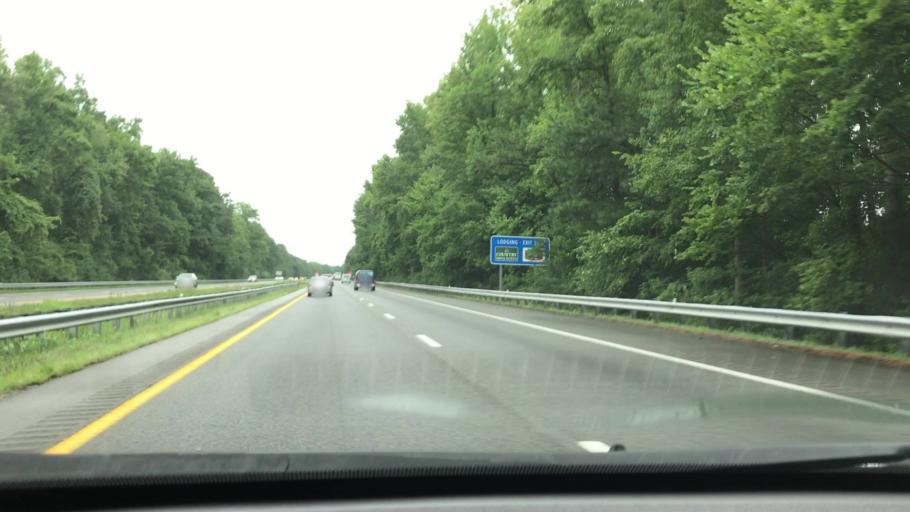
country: US
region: Virginia
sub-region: City of Emporia
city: Emporia
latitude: 36.6768
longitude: -77.5569
